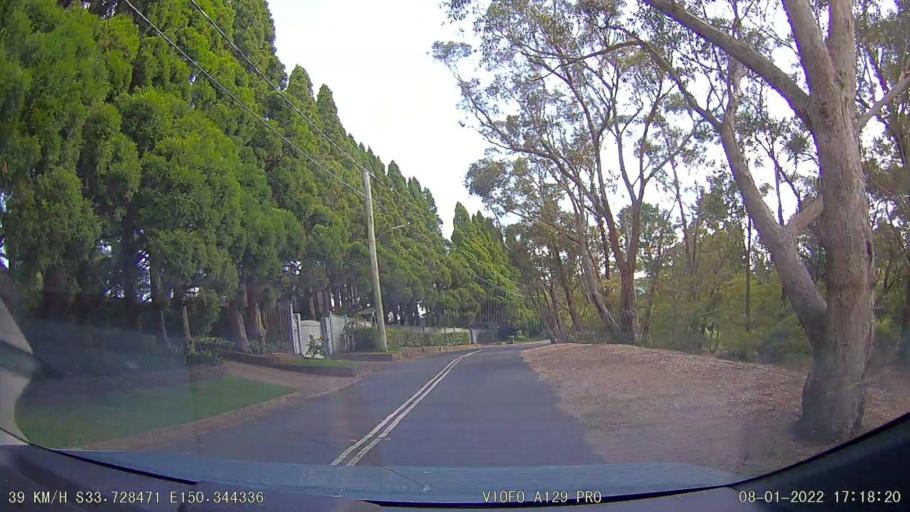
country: AU
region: New South Wales
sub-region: Blue Mountains Municipality
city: Leura
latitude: -33.7284
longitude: 150.3444
